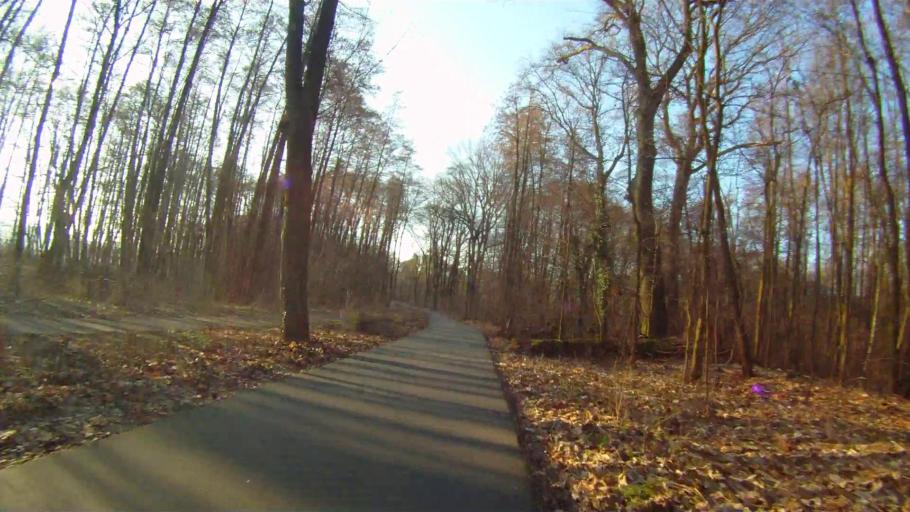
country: DE
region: Berlin
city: Friedrichshagen
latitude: 52.4397
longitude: 13.6211
